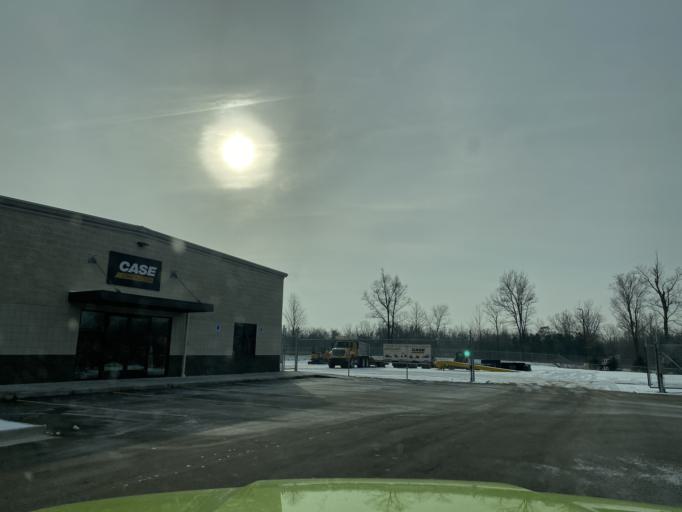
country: US
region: Michigan
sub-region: Kent County
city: Walker
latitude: 43.0359
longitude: -85.8144
